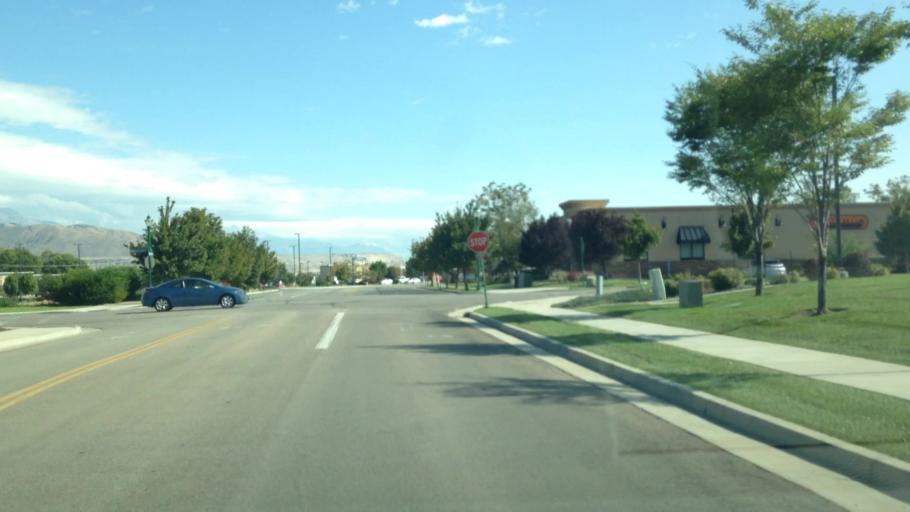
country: US
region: Utah
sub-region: Salt Lake County
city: Riverton
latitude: 40.5102
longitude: -111.9806
